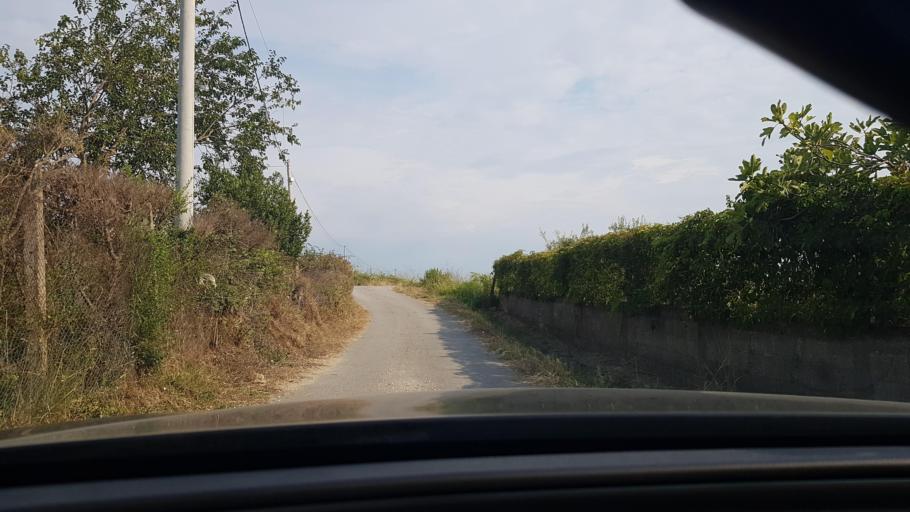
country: AL
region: Durres
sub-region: Rrethi i Durresit
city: Manze
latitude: 41.4739
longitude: 19.5659
